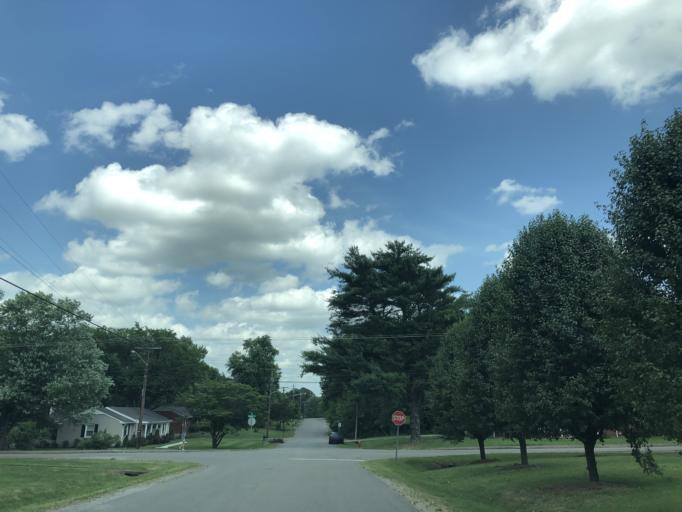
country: US
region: Tennessee
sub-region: Davidson County
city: Oak Hill
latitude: 36.0802
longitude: -86.7454
